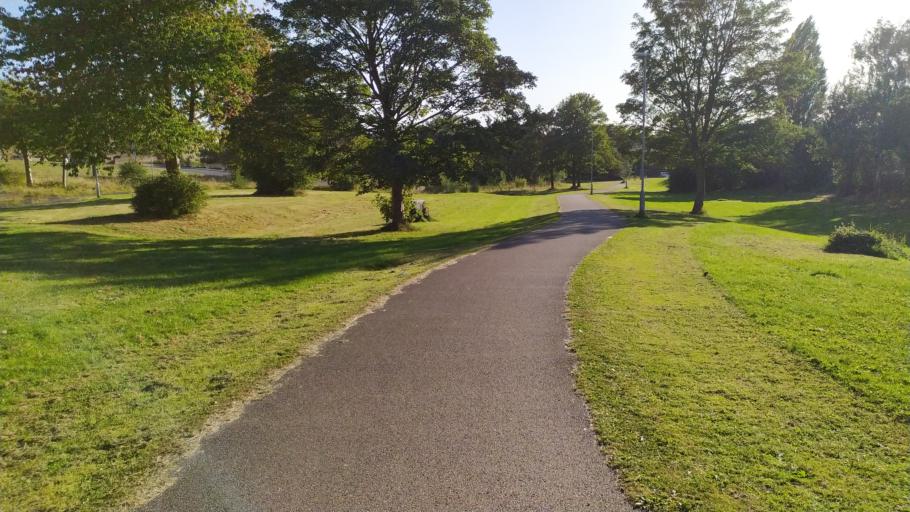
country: GB
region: England
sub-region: City and Borough of Leeds
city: Chapel Allerton
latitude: 53.8282
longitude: -1.5586
